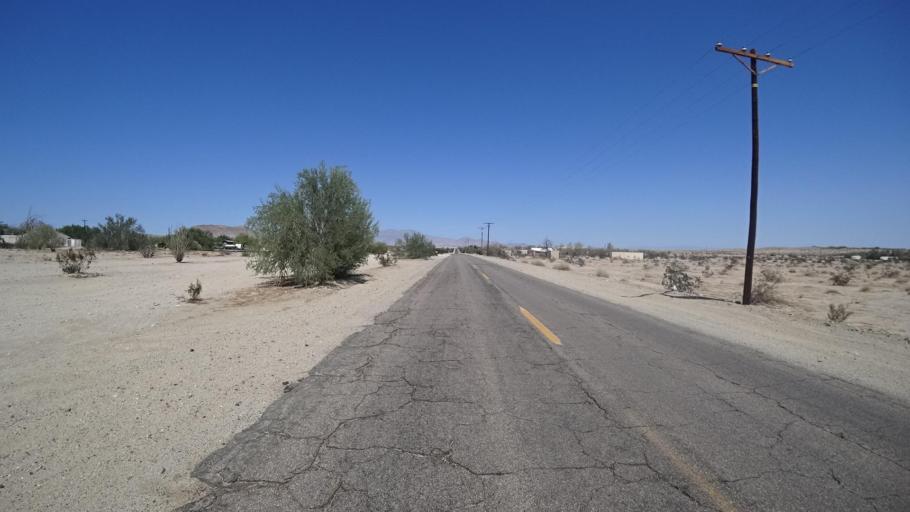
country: US
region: California
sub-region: Imperial County
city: Salton City
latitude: 33.1303
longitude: -116.1328
